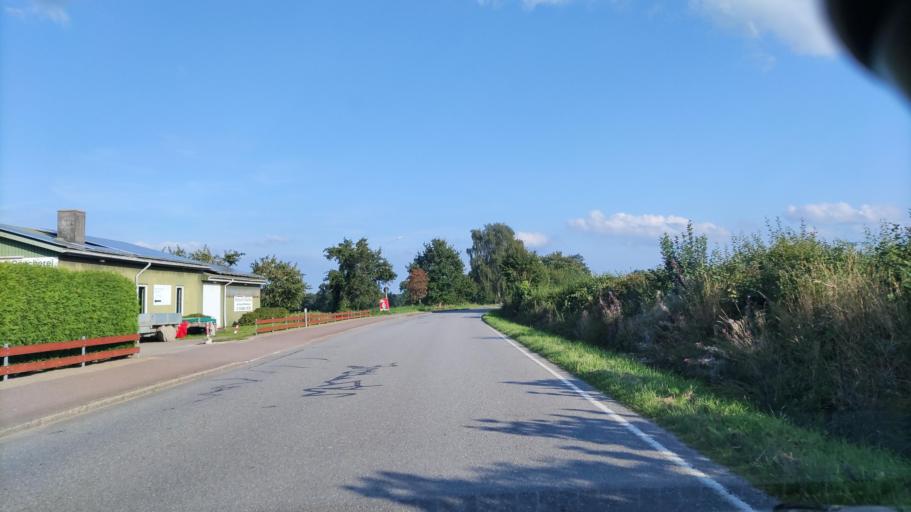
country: DE
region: Schleswig-Holstein
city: Sarlhusen
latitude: 54.0210
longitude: 9.7961
